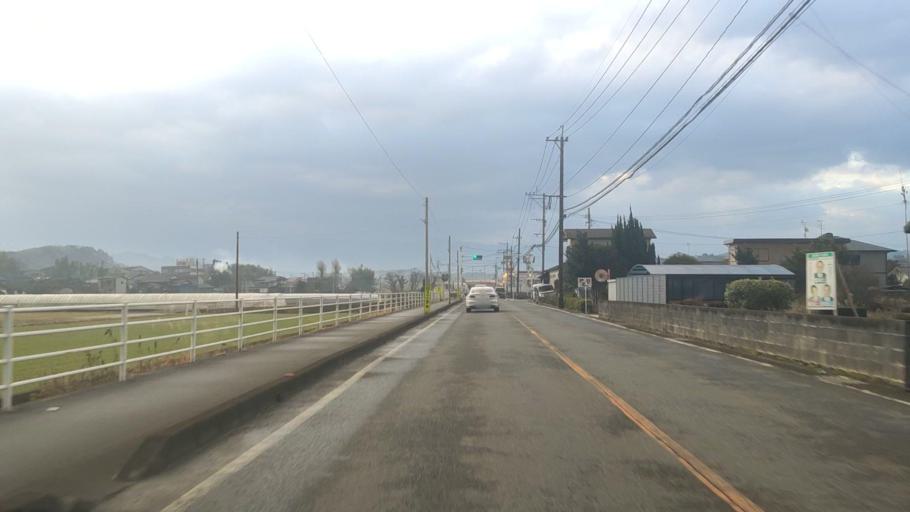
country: JP
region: Kumamoto
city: Uto
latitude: 32.7054
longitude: 130.7776
